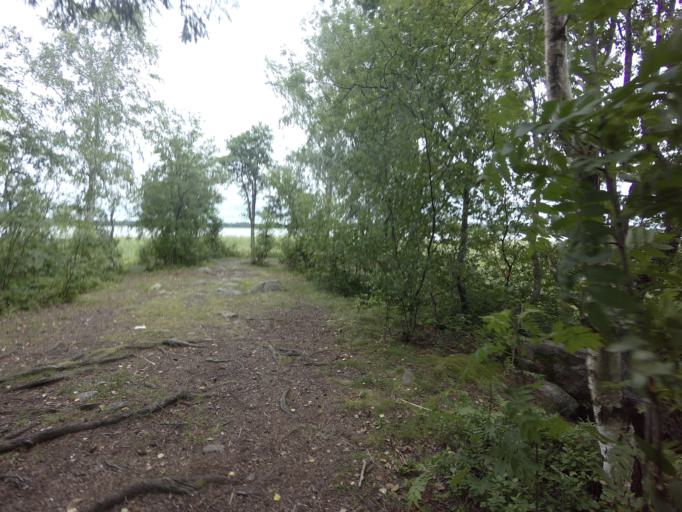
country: FI
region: Uusimaa
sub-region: Helsinki
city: Teekkarikylae
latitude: 60.1930
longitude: 24.8378
